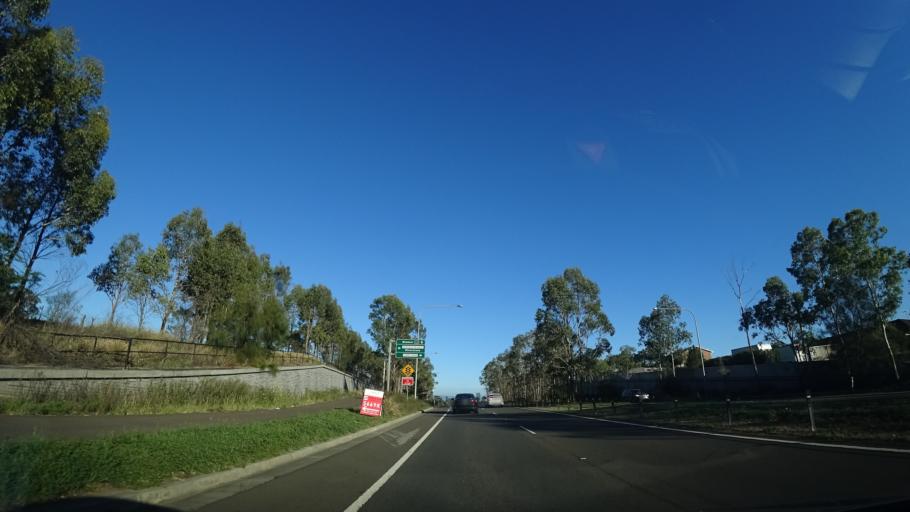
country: AU
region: New South Wales
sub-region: Blacktown
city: Rouse Hill
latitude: -33.6637
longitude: 150.8958
